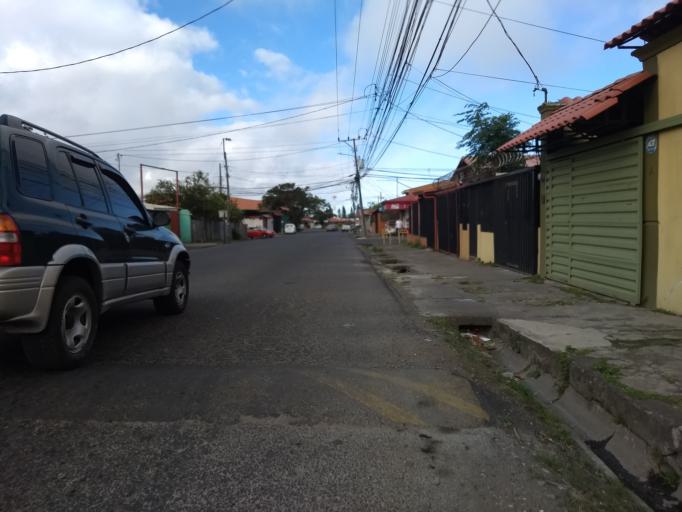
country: CR
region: San Jose
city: San Vicente de Moravia
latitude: 9.9672
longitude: -84.0481
